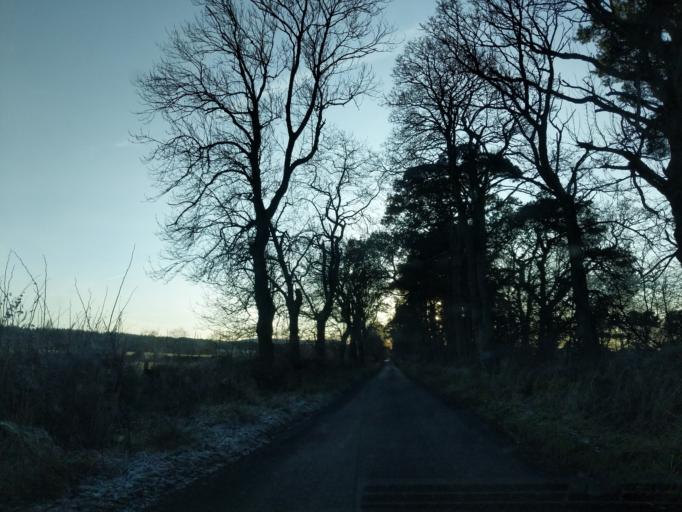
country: GB
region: Scotland
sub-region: Edinburgh
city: Balerno
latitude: 55.8717
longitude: -3.3601
